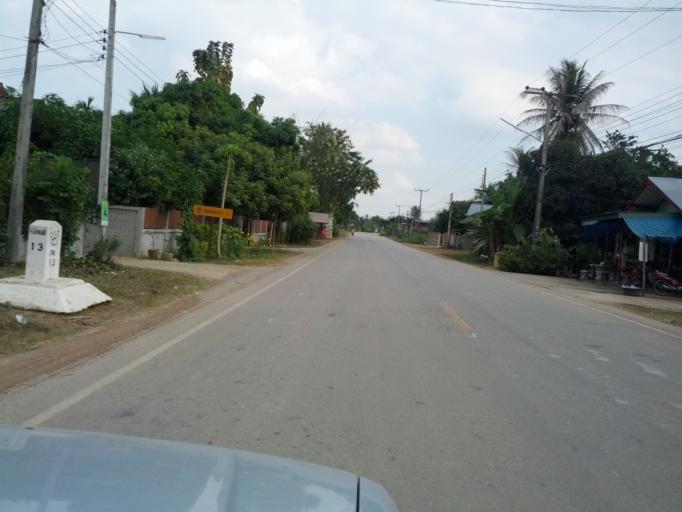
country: TH
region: Sukhothai
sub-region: Amphoe Si Satchanalai
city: Si Satchanalai
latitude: 17.4293
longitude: 99.6950
